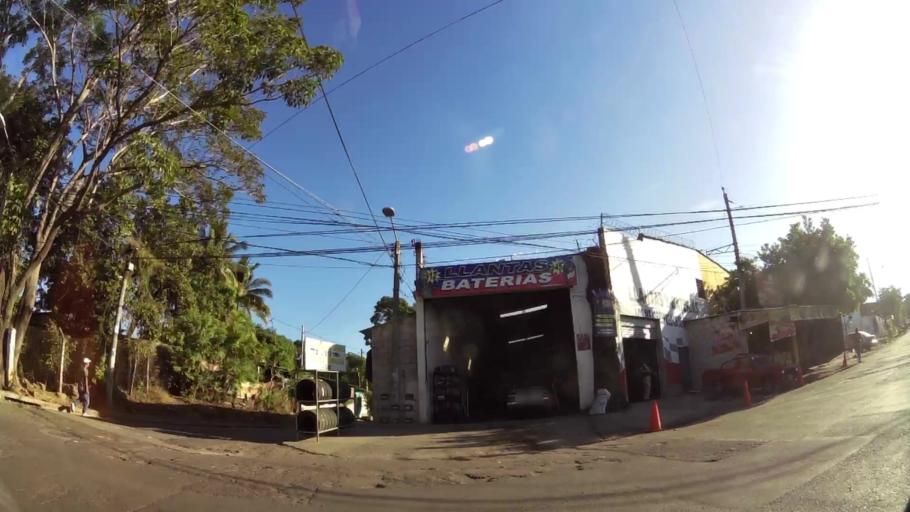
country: SV
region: Sonsonate
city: Sonsonate
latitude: 13.7139
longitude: -89.7178
